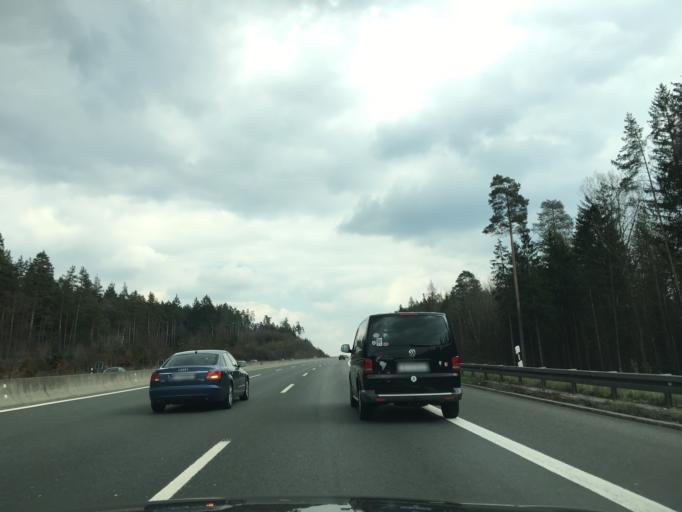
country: DE
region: Bavaria
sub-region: Upper Franconia
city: Pegnitz
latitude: 49.7215
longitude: 11.4854
